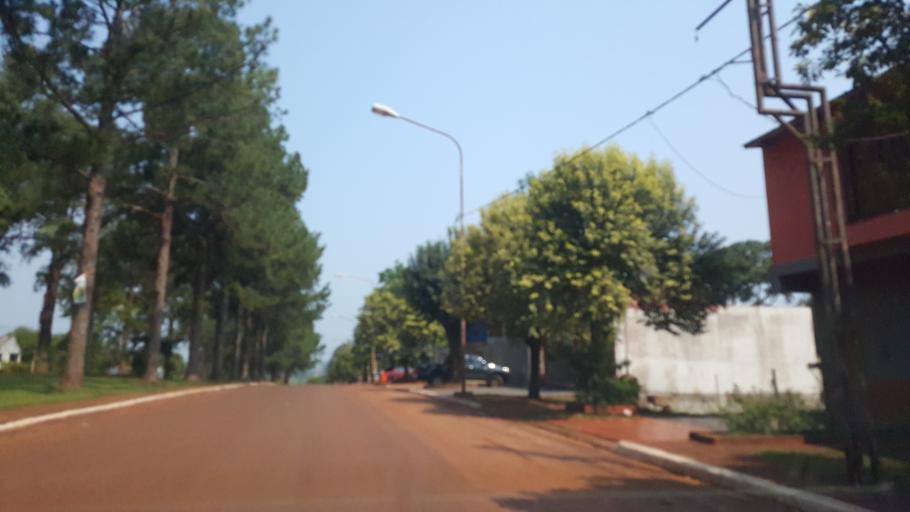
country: AR
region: Misiones
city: Santa Ana
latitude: -27.3730
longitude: -55.5791
